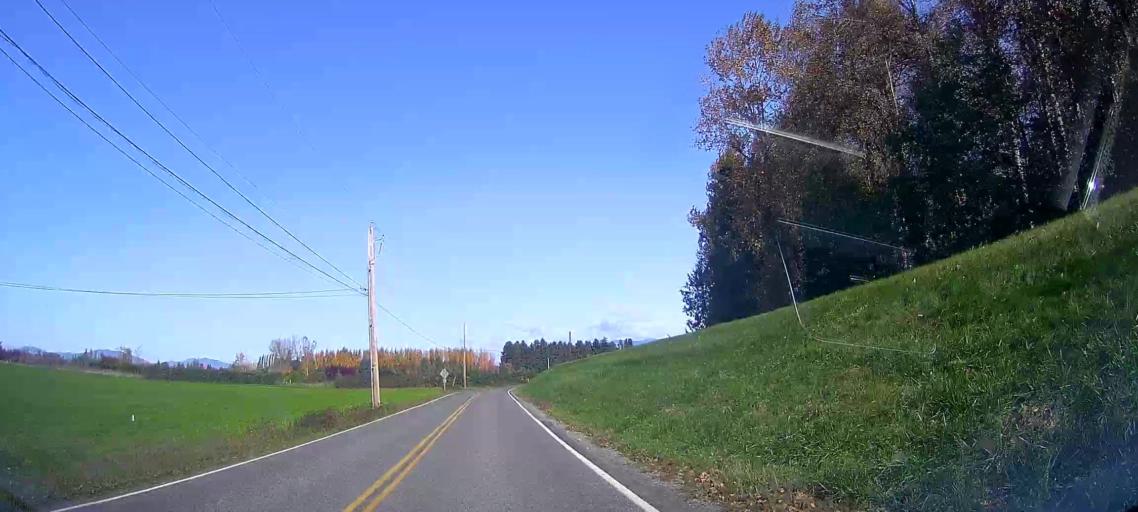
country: US
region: Washington
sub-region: Skagit County
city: Mount Vernon
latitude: 48.4125
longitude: -122.3671
